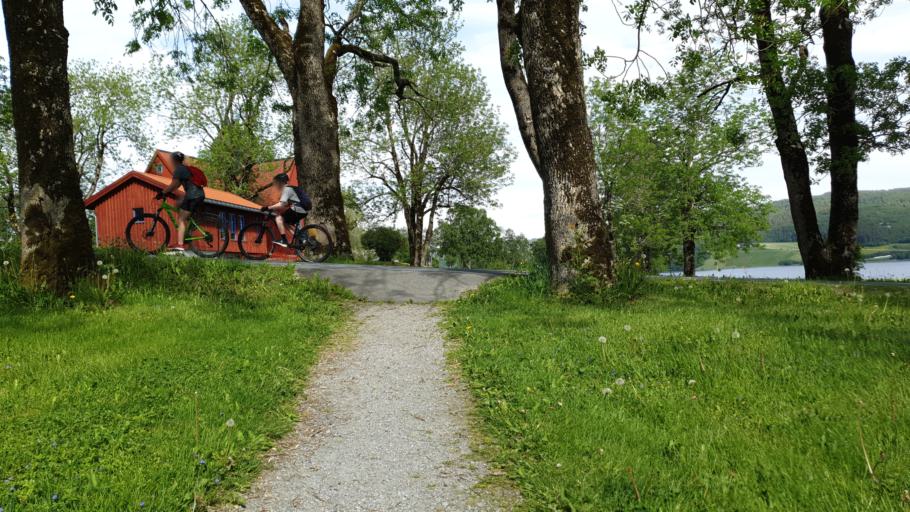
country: NO
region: Sor-Trondelag
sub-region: Rissa
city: Rissa
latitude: 63.5642
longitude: 9.9243
